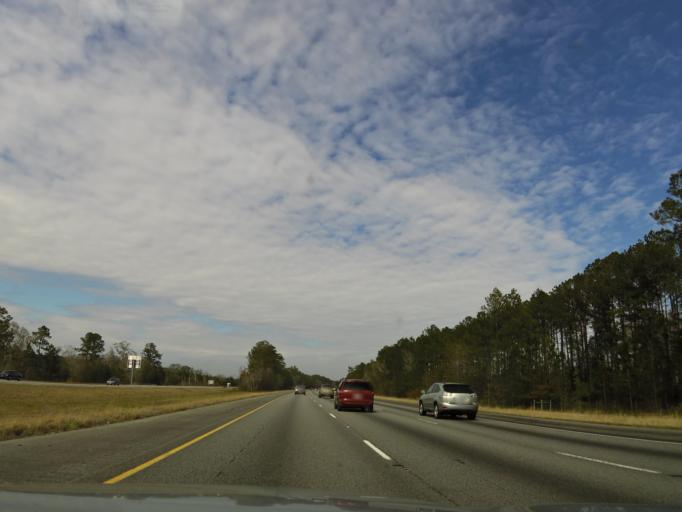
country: US
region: Georgia
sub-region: McIntosh County
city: Darien
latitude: 31.5472
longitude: -81.4442
